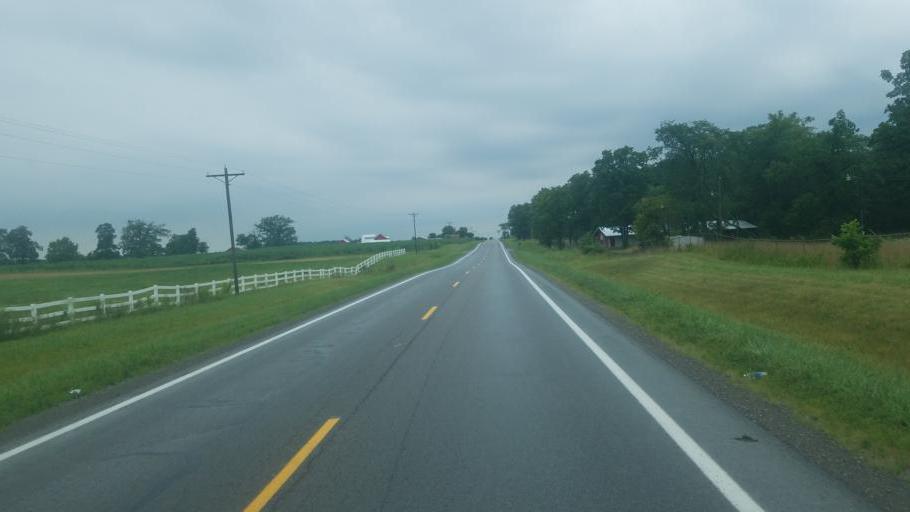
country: US
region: Ohio
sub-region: Hardin County
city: Kenton
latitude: 40.5650
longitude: -83.5891
